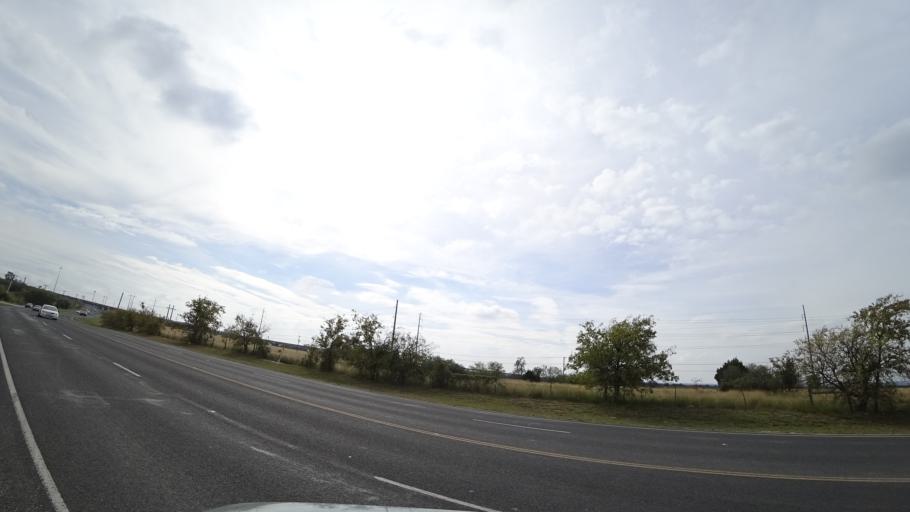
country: US
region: Texas
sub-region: Williamson County
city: Round Rock
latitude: 30.4838
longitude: -97.6943
